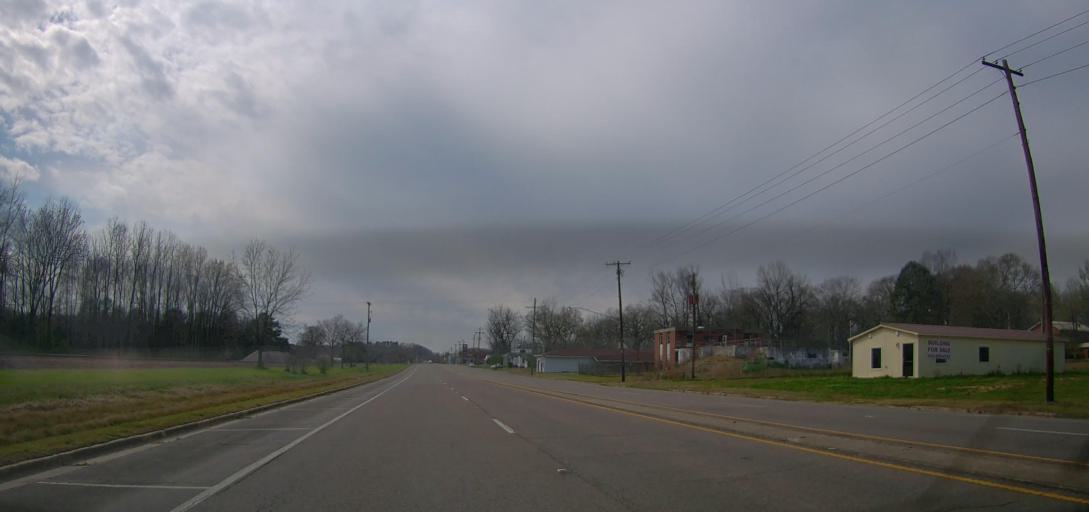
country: US
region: Alabama
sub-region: Walker County
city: Carbon Hill
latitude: 33.8868
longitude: -87.5241
